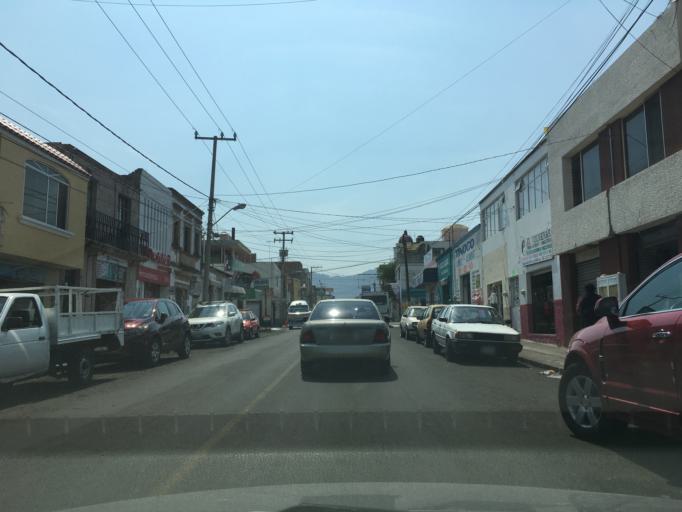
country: MX
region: Michoacan
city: Morelia
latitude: 19.7027
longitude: -101.1742
